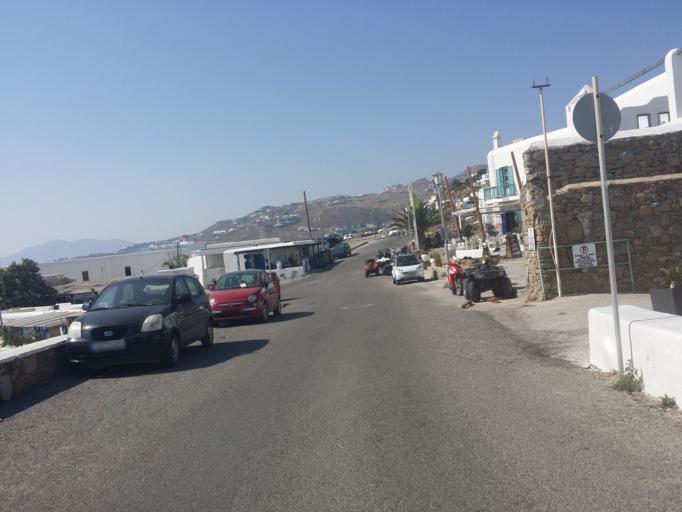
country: GR
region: South Aegean
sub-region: Nomos Kykladon
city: Mykonos
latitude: 37.4508
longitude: 25.3290
